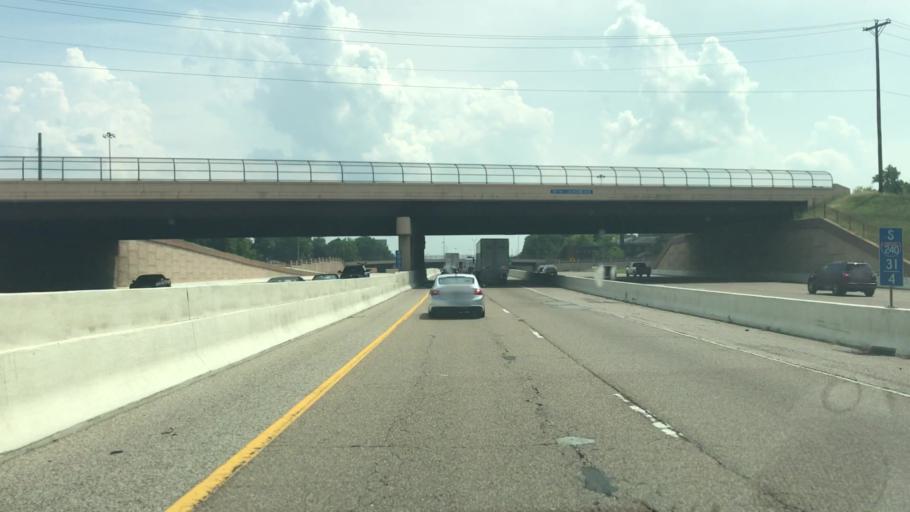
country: US
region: Tennessee
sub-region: Shelby County
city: Memphis
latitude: 35.1588
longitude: -90.0204
